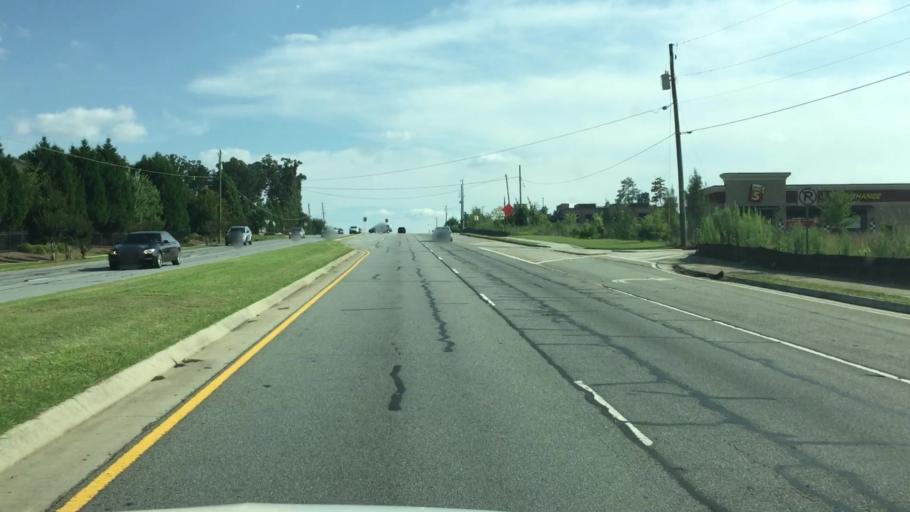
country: US
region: Georgia
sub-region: Gwinnett County
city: Grayson
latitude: 33.9083
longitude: -84.0030
